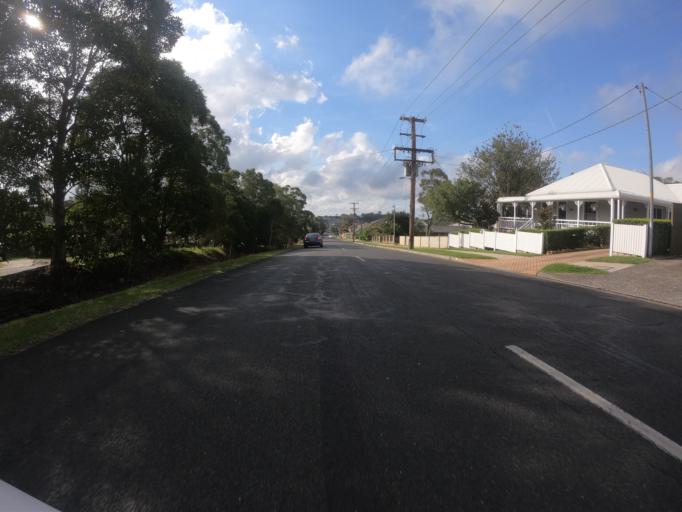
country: AU
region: New South Wales
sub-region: Wollongong
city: Helensburgh
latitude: -34.1975
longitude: 150.9808
